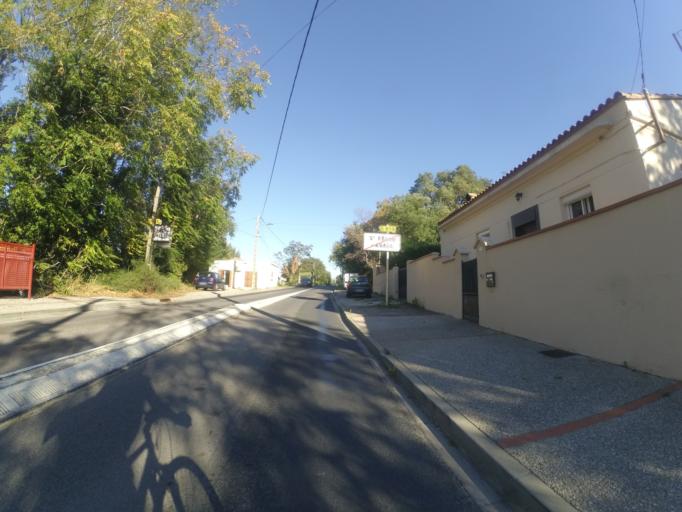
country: FR
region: Languedoc-Roussillon
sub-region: Departement des Pyrenees-Orientales
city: Corneilla-la-Riviere
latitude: 42.6818
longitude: 2.7432
